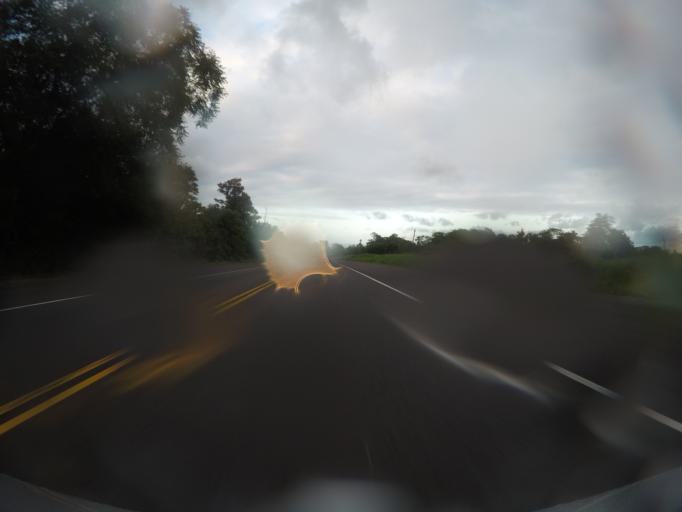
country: US
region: Hawaii
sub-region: Hawaii County
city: Hilo
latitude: 19.6838
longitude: -155.1204
